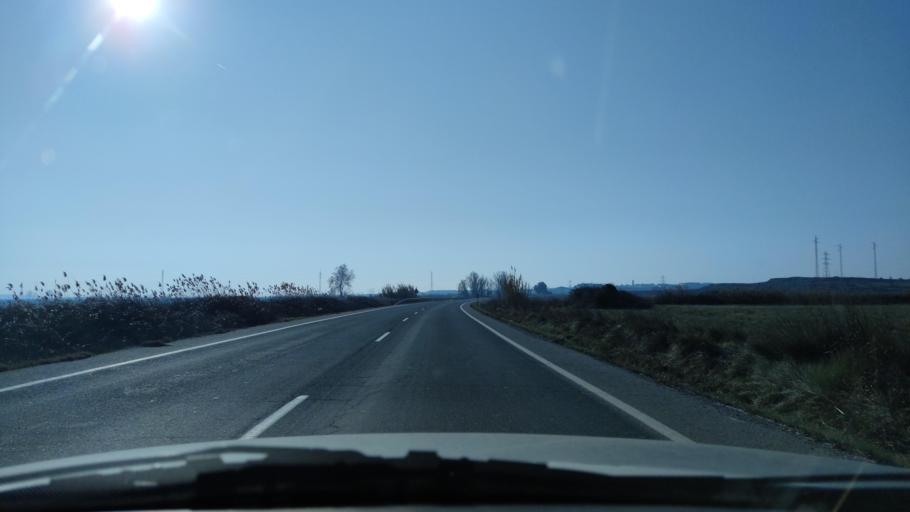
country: ES
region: Catalonia
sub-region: Provincia de Lleida
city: Albesa
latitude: 41.7146
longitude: 0.6394
